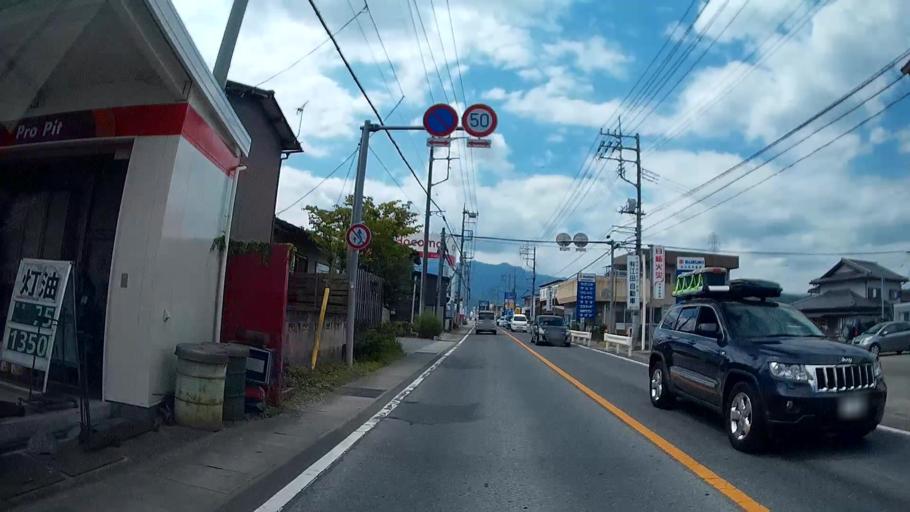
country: JP
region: Saitama
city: Chichibu
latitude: 35.9823
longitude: 139.0782
